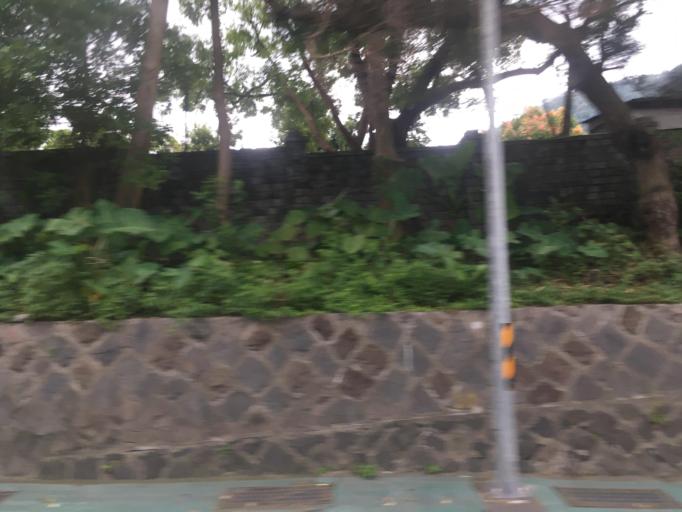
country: TW
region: Taipei
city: Taipei
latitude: 25.1368
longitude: 121.5286
